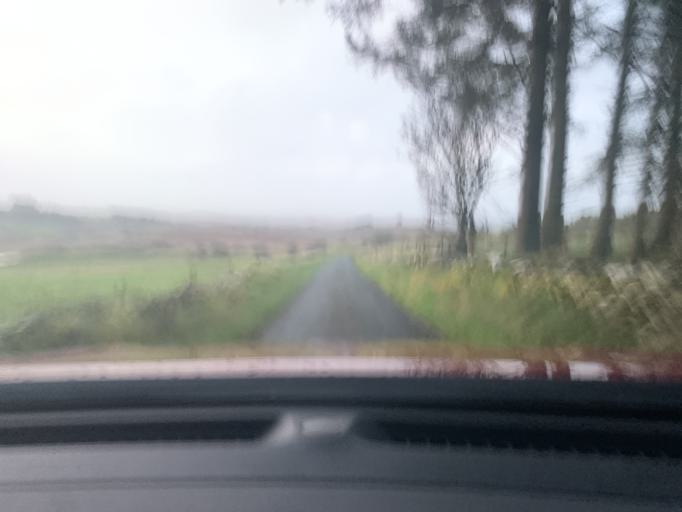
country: IE
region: Connaught
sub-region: Sligo
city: Ballymote
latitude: 54.0598
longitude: -8.3978
